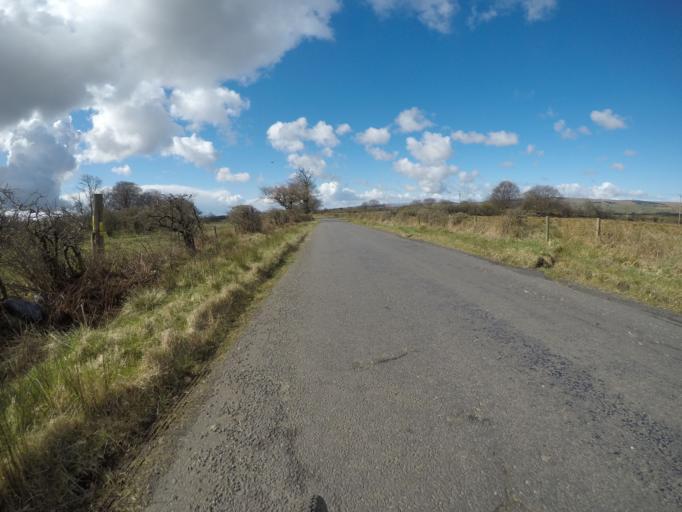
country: GB
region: Scotland
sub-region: North Ayrshire
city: Kilbirnie
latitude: 55.7191
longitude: -4.6755
